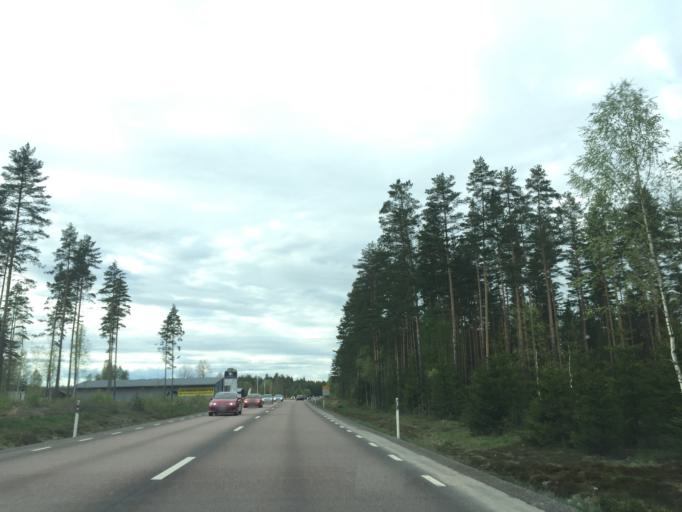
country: SE
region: Vaermland
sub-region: Eda Kommun
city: Charlottenberg
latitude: 59.8895
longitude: 12.2812
